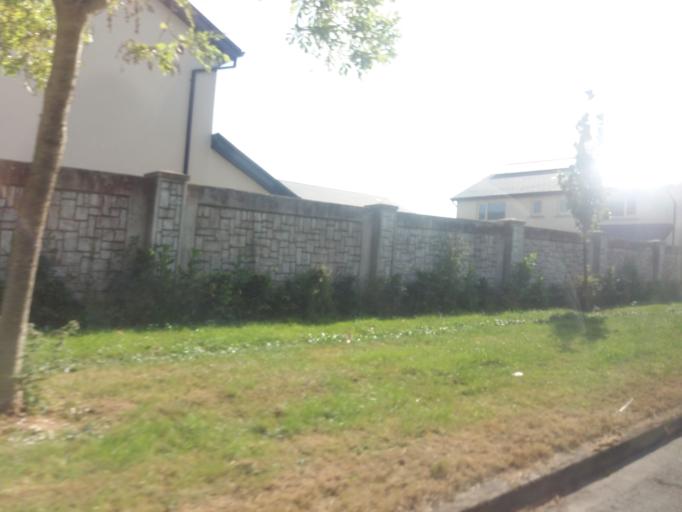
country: IE
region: Leinster
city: Lusk
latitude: 53.5214
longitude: -6.1661
